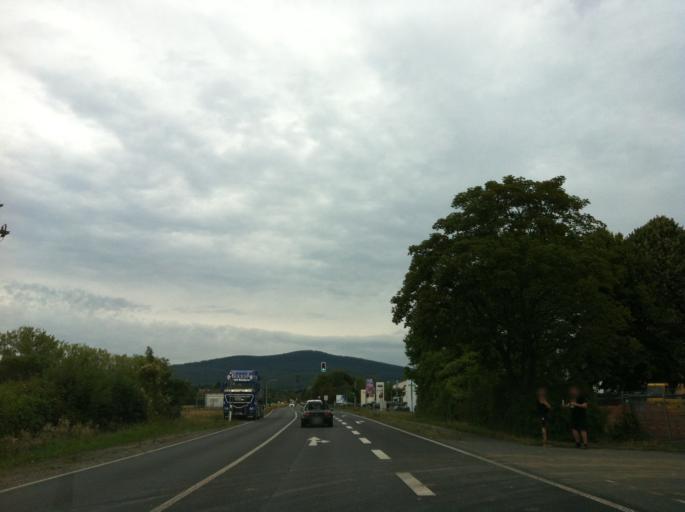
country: DE
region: Hesse
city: Schwalbach am Taunus
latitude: 50.1665
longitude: 8.5333
